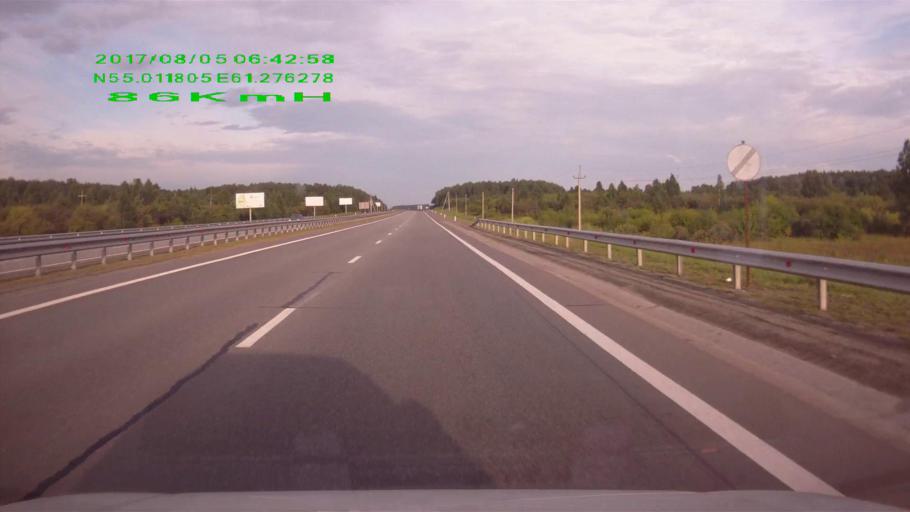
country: RU
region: Chelyabinsk
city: Sargazy
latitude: 55.0118
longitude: 61.2756
